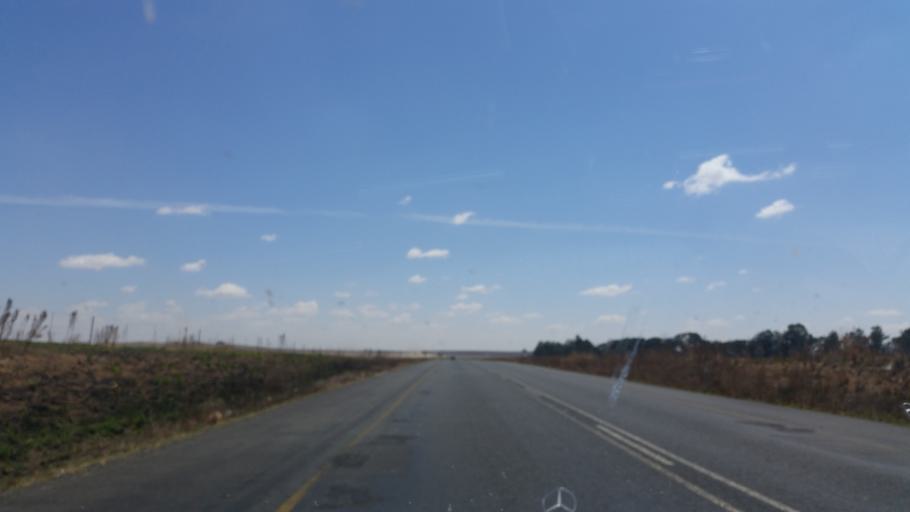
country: ZA
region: Orange Free State
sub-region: Thabo Mofutsanyana District Municipality
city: Bethlehem
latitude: -28.1087
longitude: 28.6669
